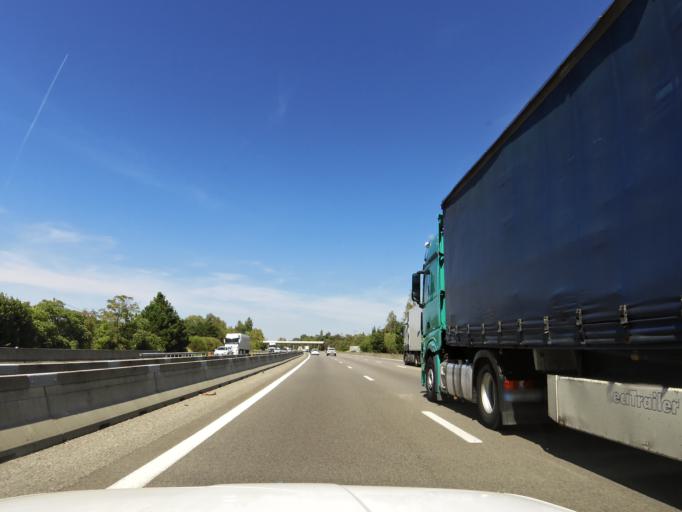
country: FR
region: Rhone-Alpes
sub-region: Departement de l'Ardeche
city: Guilherand-Granges
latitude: 44.9097
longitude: 4.8771
